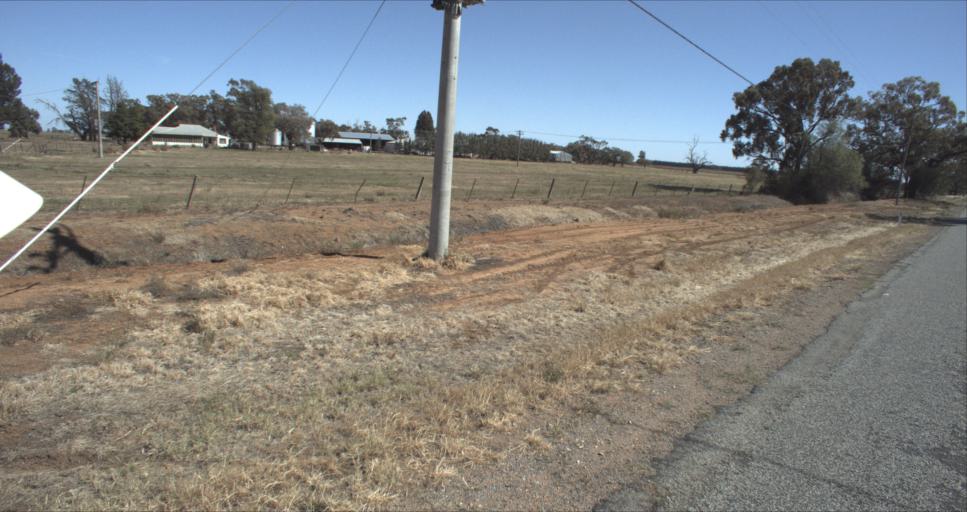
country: AU
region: New South Wales
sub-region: Leeton
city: Leeton
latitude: -34.5444
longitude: 146.3159
